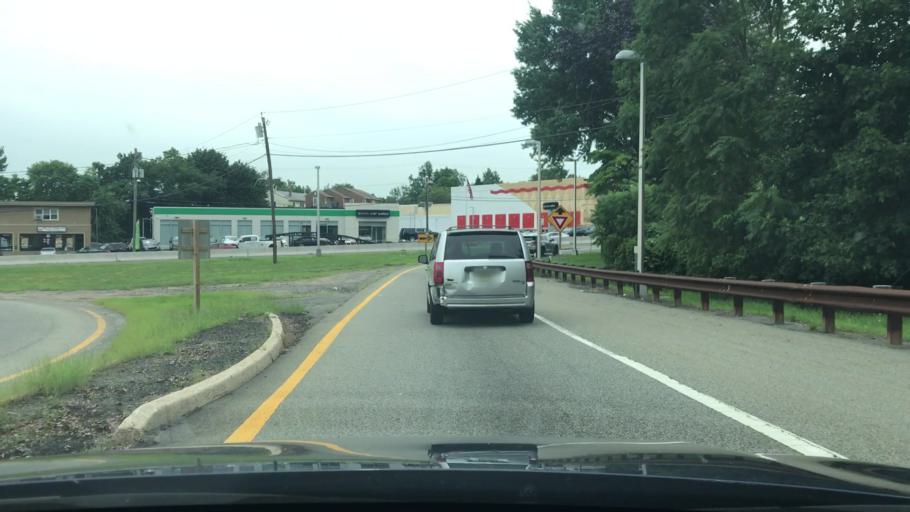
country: US
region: New Jersey
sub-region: Bergen County
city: Elmwood Park
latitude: 40.8940
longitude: -74.1214
